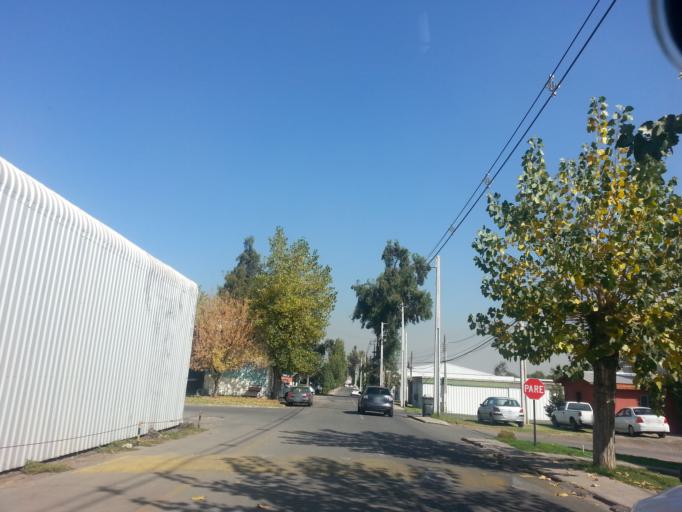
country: CL
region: Santiago Metropolitan
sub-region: Provincia de Santiago
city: Villa Presidente Frei, Nunoa, Santiago, Chile
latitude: -33.4594
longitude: -70.5500
